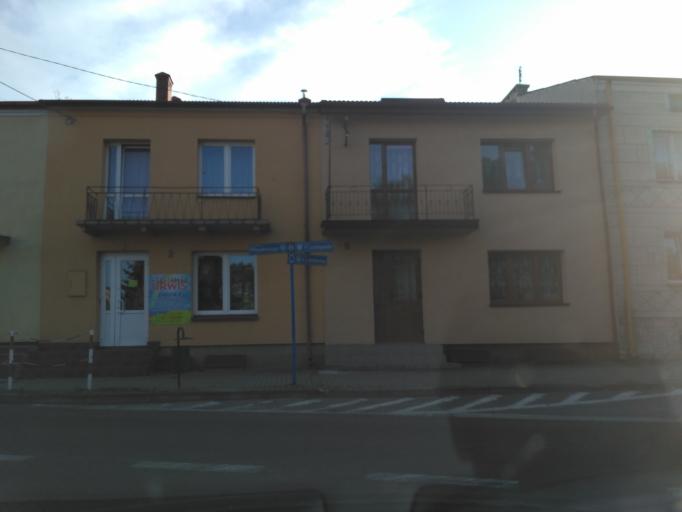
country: PL
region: Lublin Voivodeship
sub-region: Powiat lubelski
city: Bychawa
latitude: 51.0160
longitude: 22.5330
